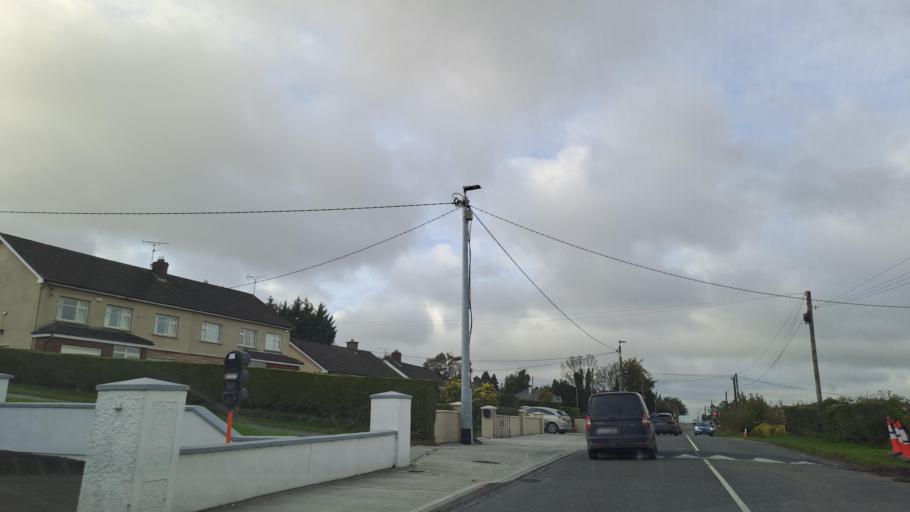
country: IE
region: Ulster
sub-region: An Cabhan
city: Kingscourt
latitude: 53.8982
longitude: -6.8029
